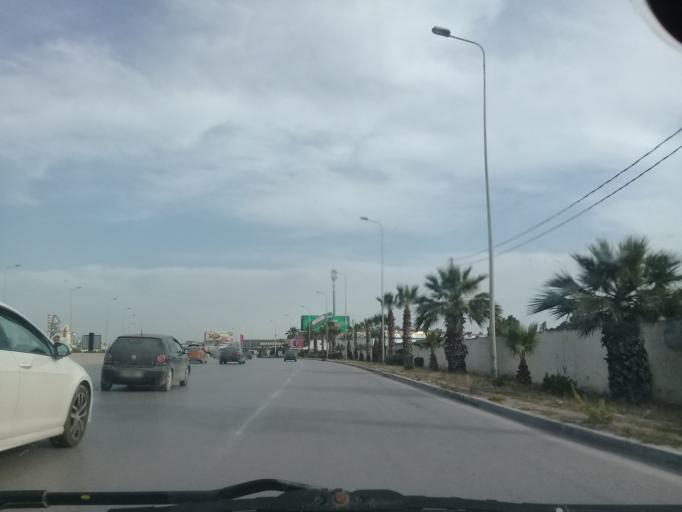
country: TN
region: Tunis
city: Tunis
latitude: 36.7892
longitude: 10.1916
